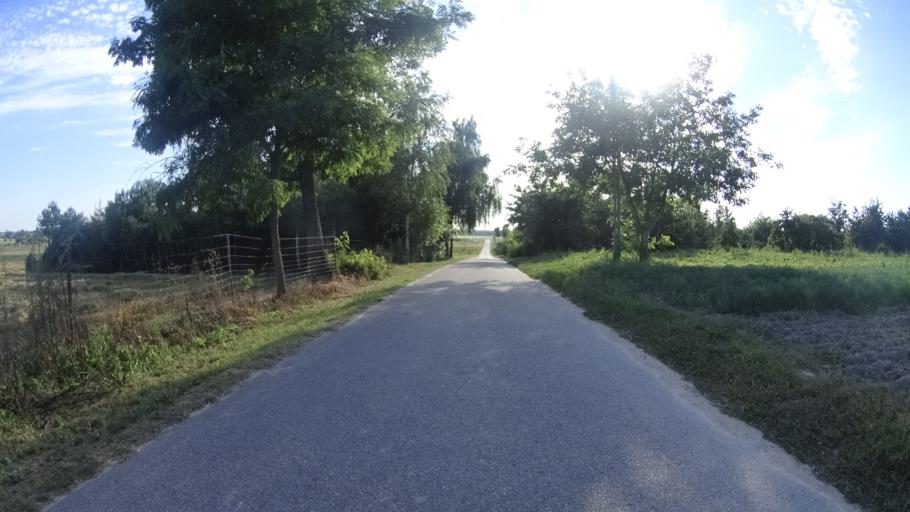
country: PL
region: Masovian Voivodeship
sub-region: Powiat grojecki
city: Goszczyn
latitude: 51.6831
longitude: 20.8310
